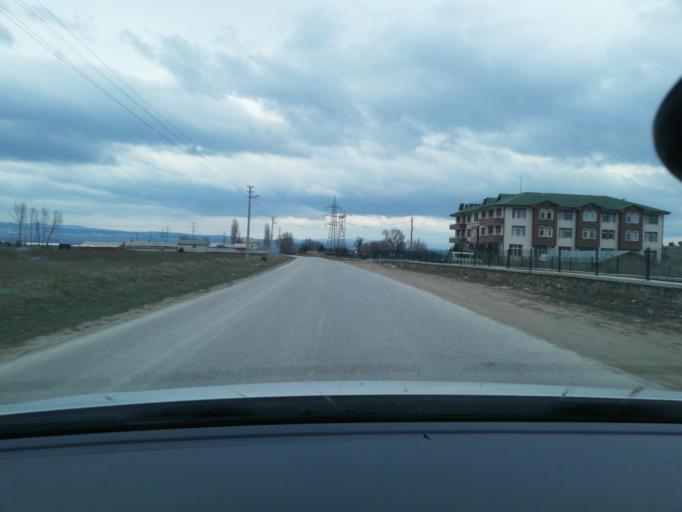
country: TR
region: Bolu
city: Gerede
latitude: 40.7834
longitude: 32.2045
